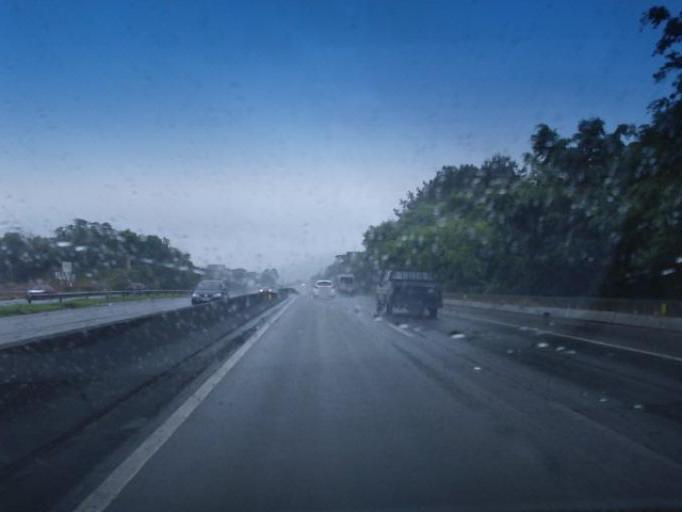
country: BR
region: Santa Catarina
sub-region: Joinville
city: Joinville
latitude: -26.3354
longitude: -48.8600
